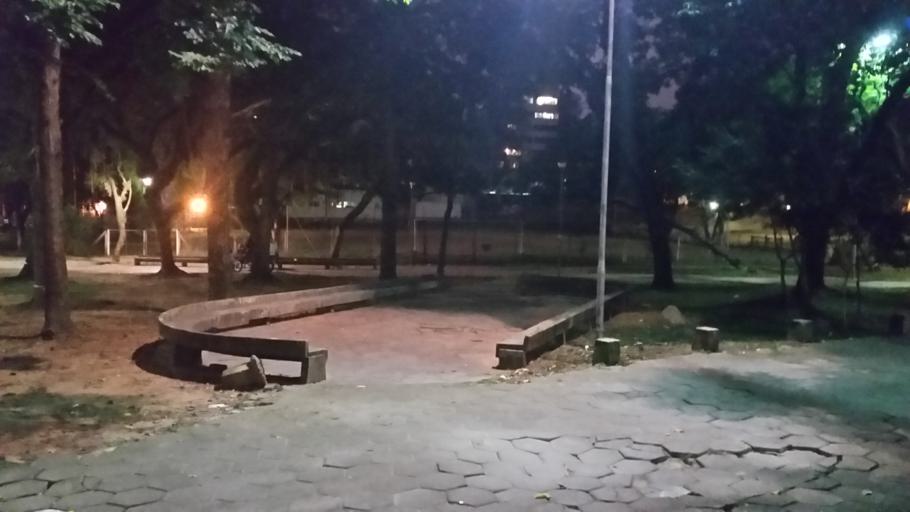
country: BR
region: Rio Grande do Sul
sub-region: Porto Alegre
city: Porto Alegre
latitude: -30.0425
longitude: -51.1822
